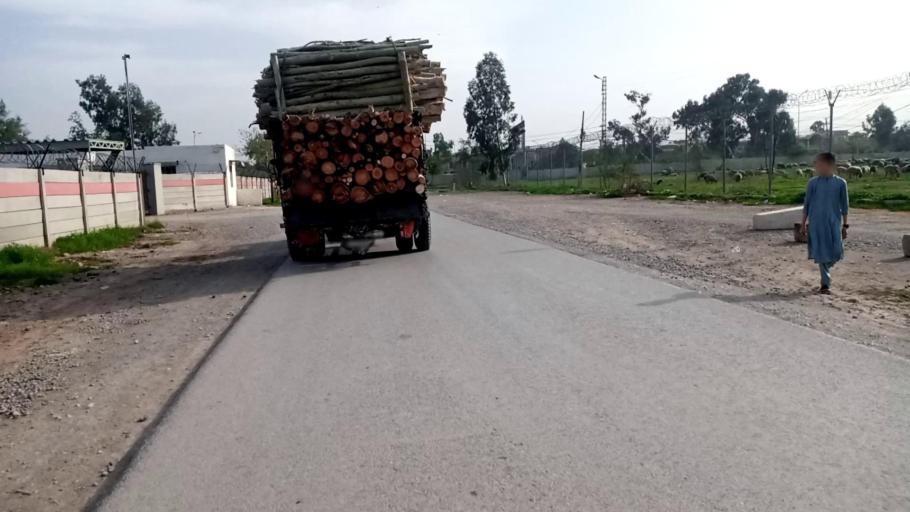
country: PK
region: Khyber Pakhtunkhwa
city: Peshawar
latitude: 33.9982
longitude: 71.4524
